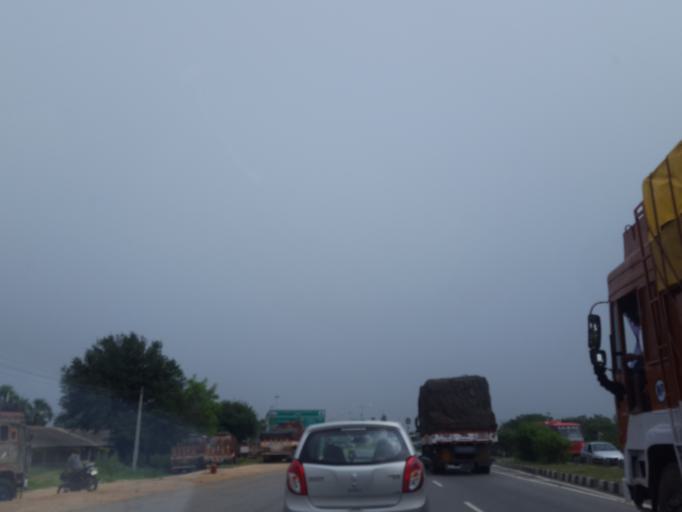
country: IN
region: Telangana
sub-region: Nalgonda
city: Gudur
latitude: 17.2350
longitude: 78.9539
